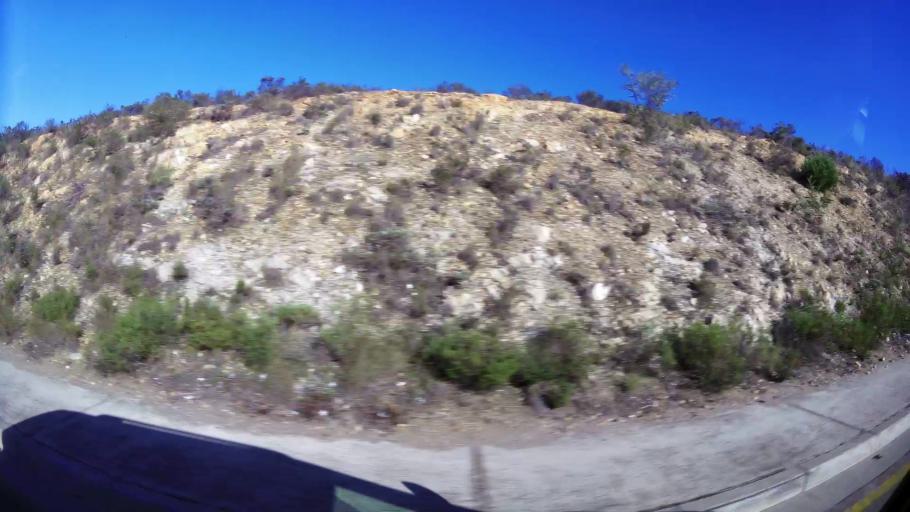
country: ZA
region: Eastern Cape
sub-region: Nelson Mandela Bay Metropolitan Municipality
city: Port Elizabeth
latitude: -33.9803
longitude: 25.6351
